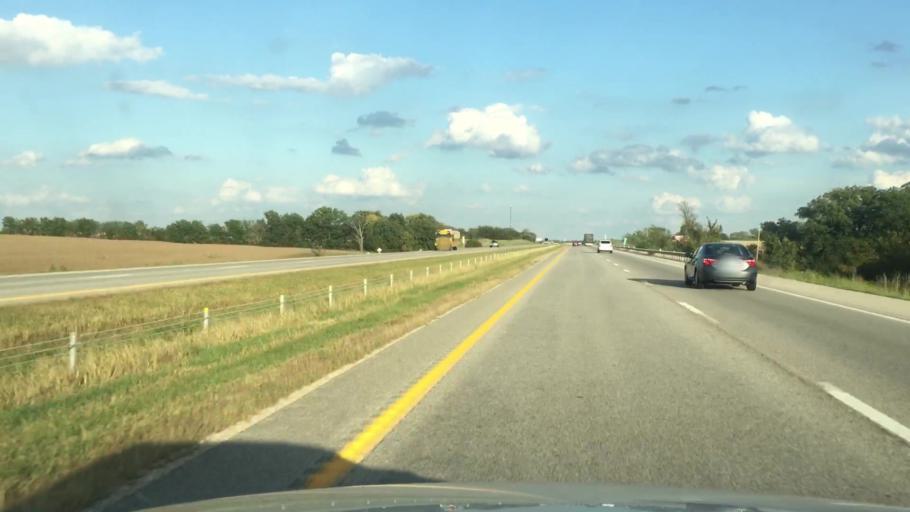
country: US
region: Missouri
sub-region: Saline County
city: Sweet Springs
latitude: 38.9718
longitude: -93.2907
